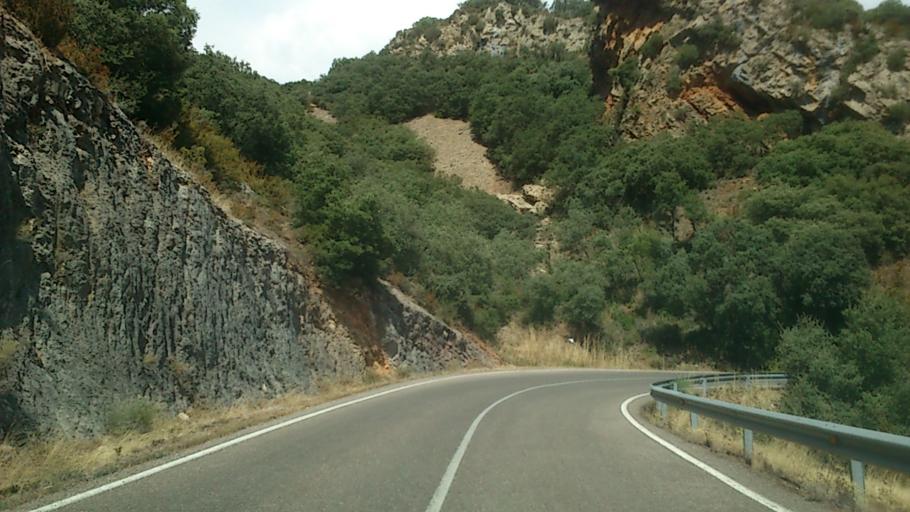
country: ES
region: Castille and Leon
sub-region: Provincia de Burgos
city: Frias
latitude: 42.7504
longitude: -3.3058
